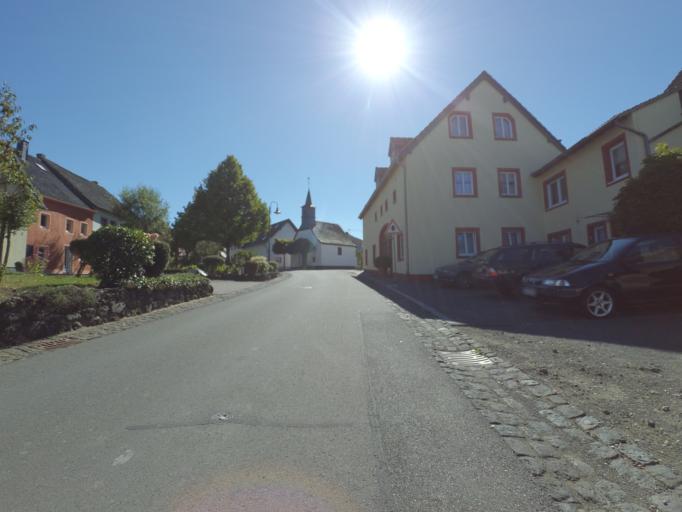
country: DE
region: Rheinland-Pfalz
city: Daun
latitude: 50.2055
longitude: 6.8471
